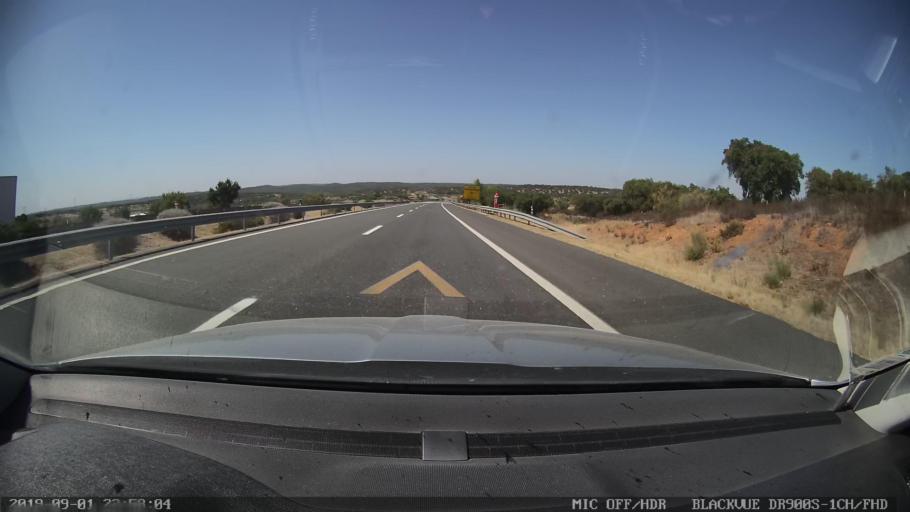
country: PT
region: Evora
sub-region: Estremoz
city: Estremoz
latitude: 38.7535
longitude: -7.7184
